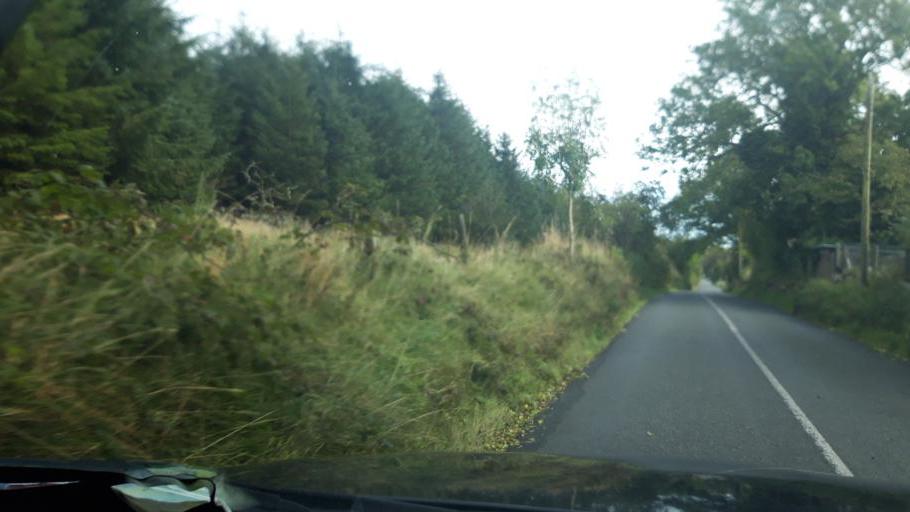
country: IE
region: Leinster
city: Ballinteer
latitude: 53.2271
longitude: -6.2582
